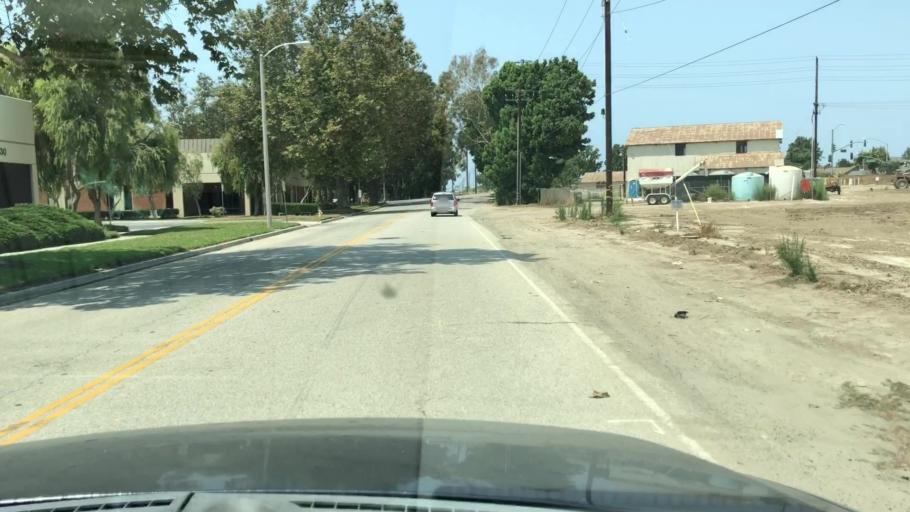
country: US
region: California
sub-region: Ventura County
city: Camarillo
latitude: 34.2052
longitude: -119.0101
